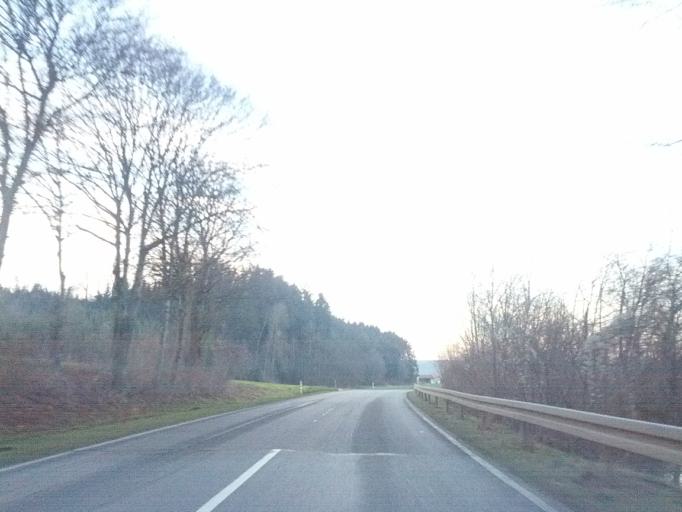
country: DE
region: Bavaria
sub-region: Swabia
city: Lautrach
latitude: 47.9191
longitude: 10.1077
